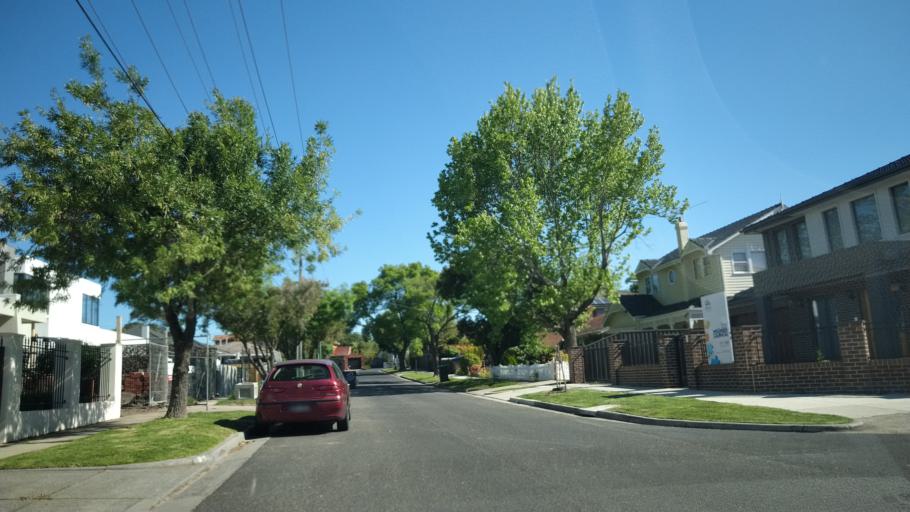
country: AU
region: Victoria
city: Ormond
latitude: -37.9054
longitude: 145.0280
